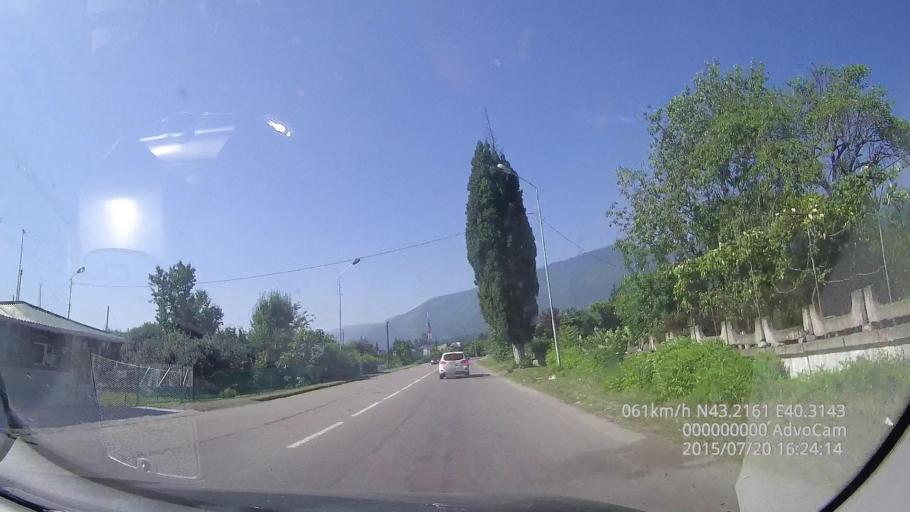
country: GE
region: Abkhazia
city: Bich'vinta
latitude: 43.2161
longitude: 40.3143
